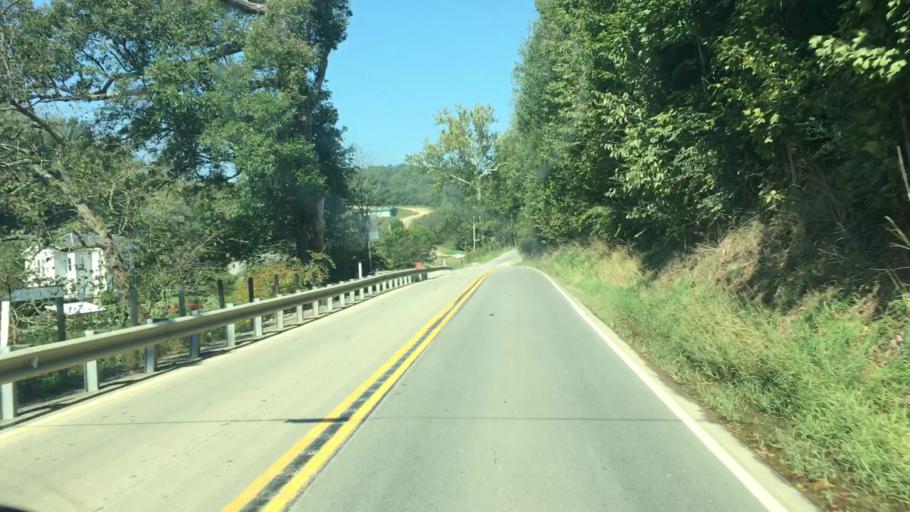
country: US
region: Pennsylvania
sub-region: Greene County
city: Waynesburg
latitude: 39.9677
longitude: -80.3163
